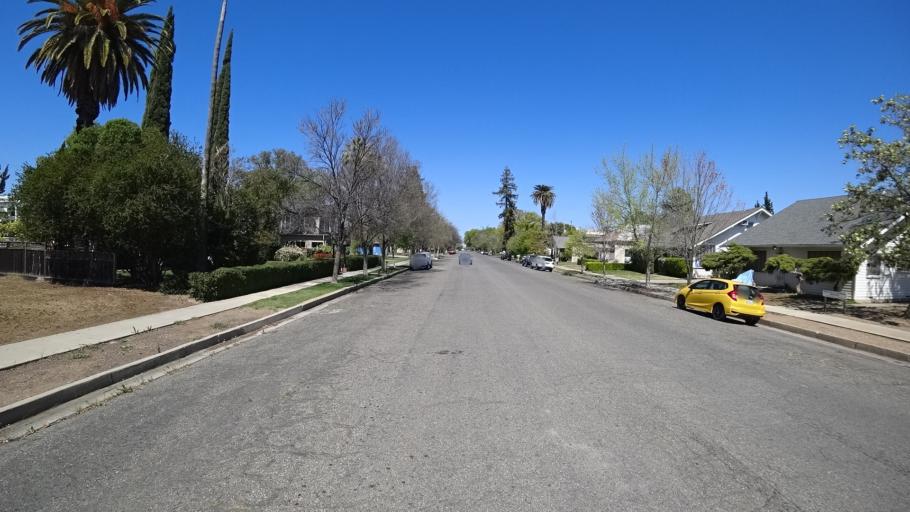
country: US
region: California
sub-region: Glenn County
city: Willows
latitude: 39.5208
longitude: -122.1983
